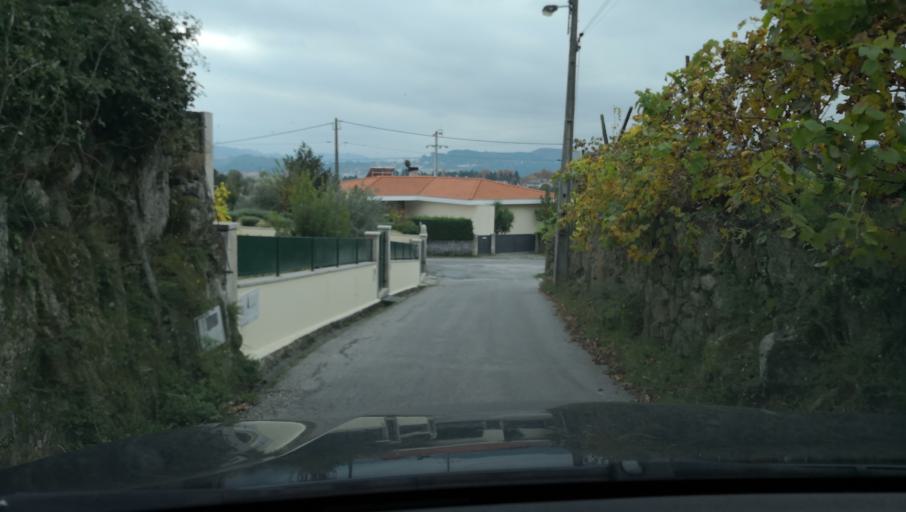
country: PT
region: Vila Real
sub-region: Vila Real
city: Vila Real
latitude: 41.3212
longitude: -7.7629
